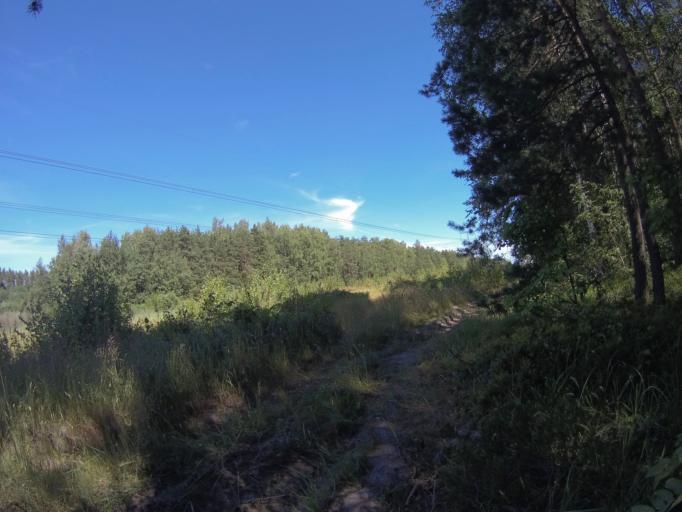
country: RU
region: Vladimir
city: Kommunar
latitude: 56.0584
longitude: 40.4484
